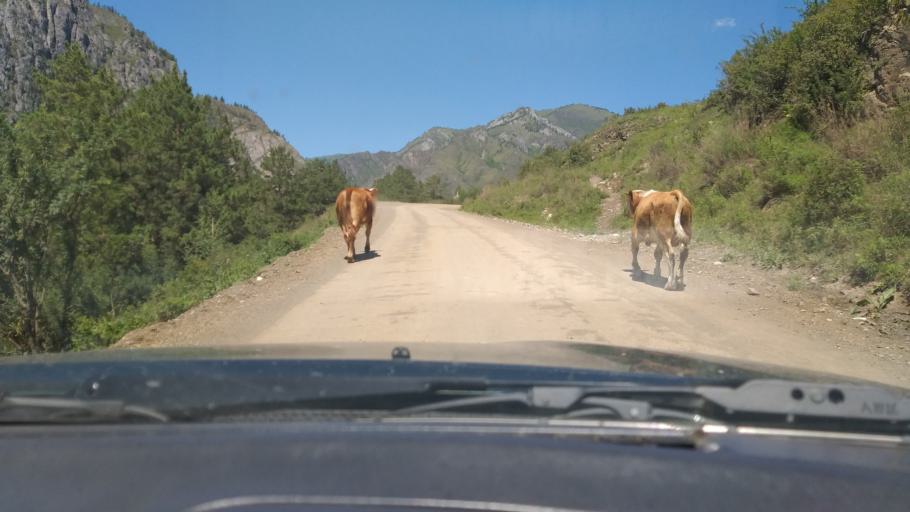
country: RU
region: Altay
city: Chemal
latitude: 51.2061
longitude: 86.0855
